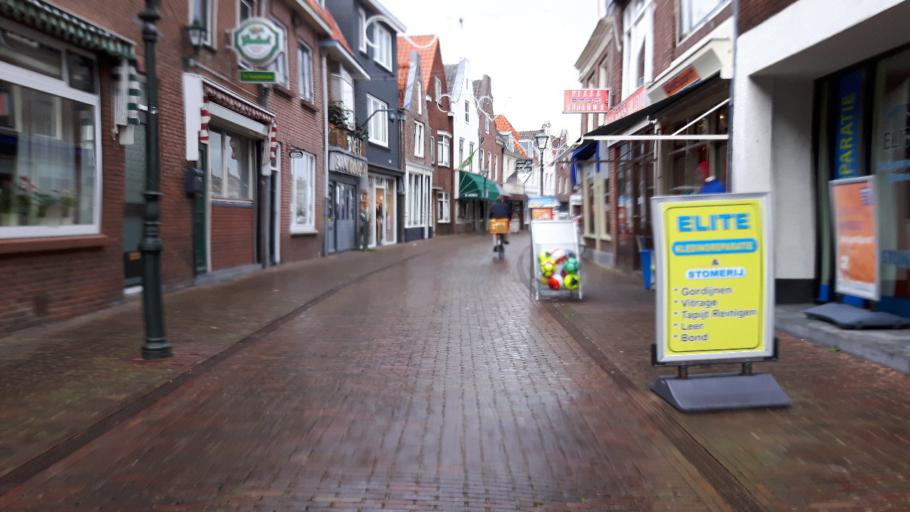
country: NL
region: Utrecht
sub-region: Stichtse Vecht
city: Maarssen
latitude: 52.1409
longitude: 5.0396
